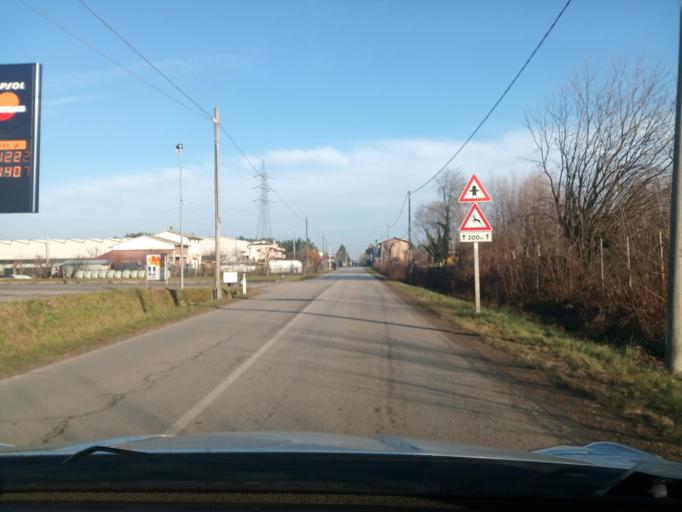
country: IT
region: Veneto
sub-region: Provincia di Vicenza
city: Novoledo
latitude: 45.6399
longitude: 11.5292
